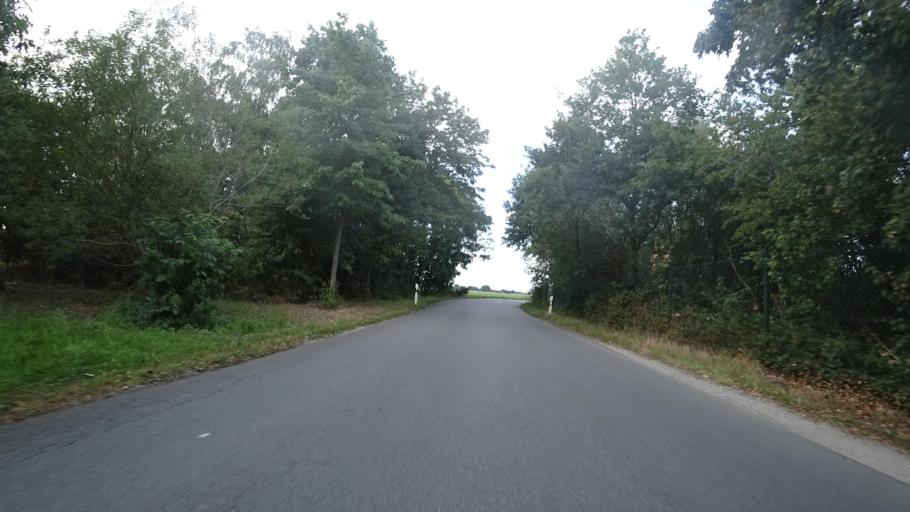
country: DE
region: North Rhine-Westphalia
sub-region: Regierungsbezirk Detmold
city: Rheda-Wiedenbruck
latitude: 51.8679
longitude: 8.2964
